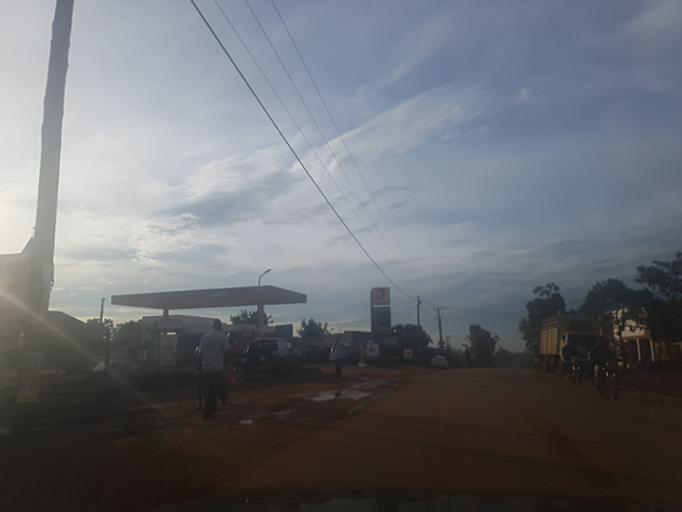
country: UG
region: Central Region
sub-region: Wakiso District
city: Bweyogerere
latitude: 0.3754
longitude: 32.7099
